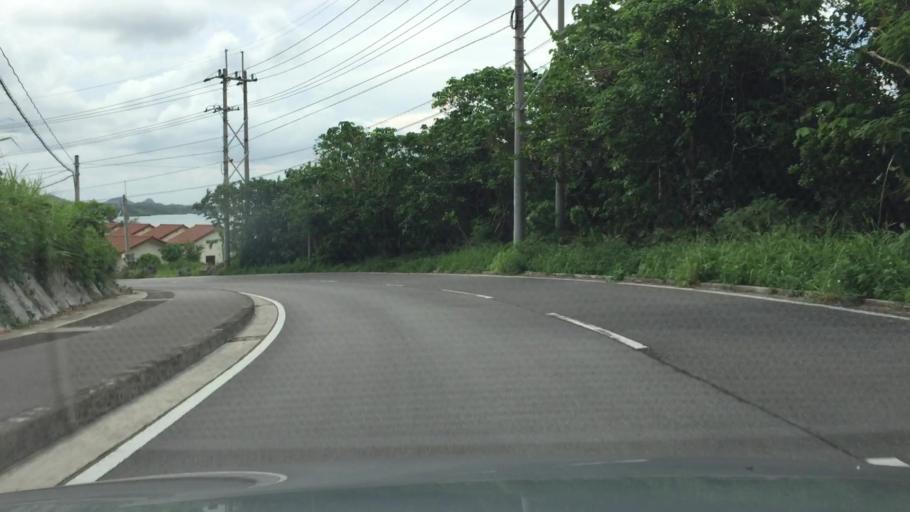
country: JP
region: Okinawa
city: Ishigaki
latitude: 24.4504
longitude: 124.1649
